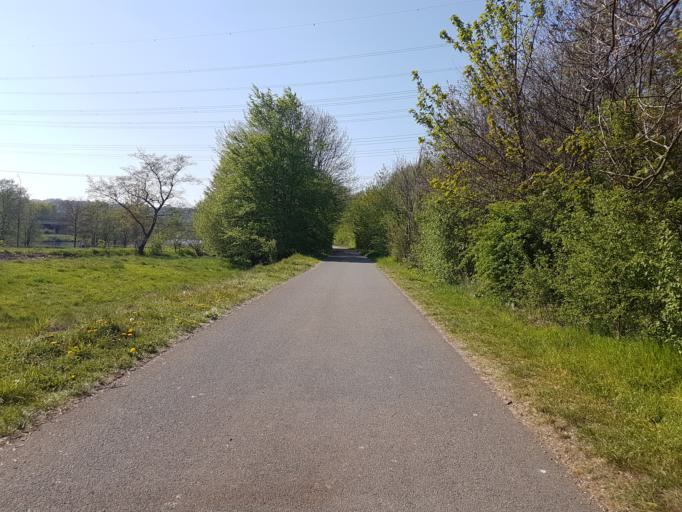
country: DE
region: North Rhine-Westphalia
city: Witten
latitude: 51.4309
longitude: 7.2867
